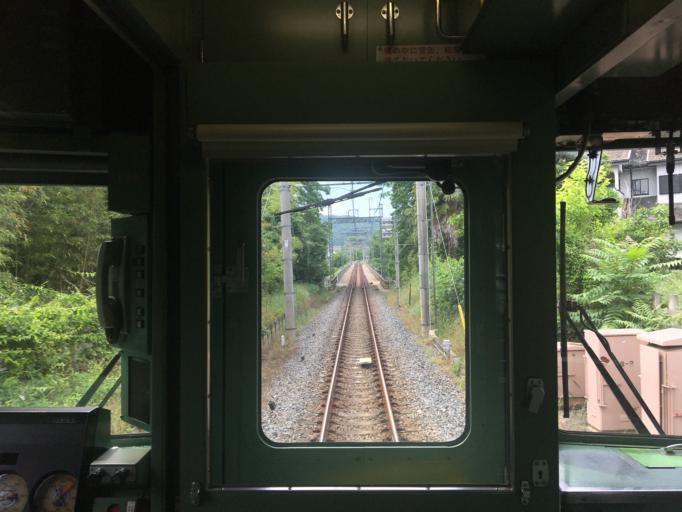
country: JP
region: Saitama
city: Yorii
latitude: 36.1144
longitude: 139.2042
